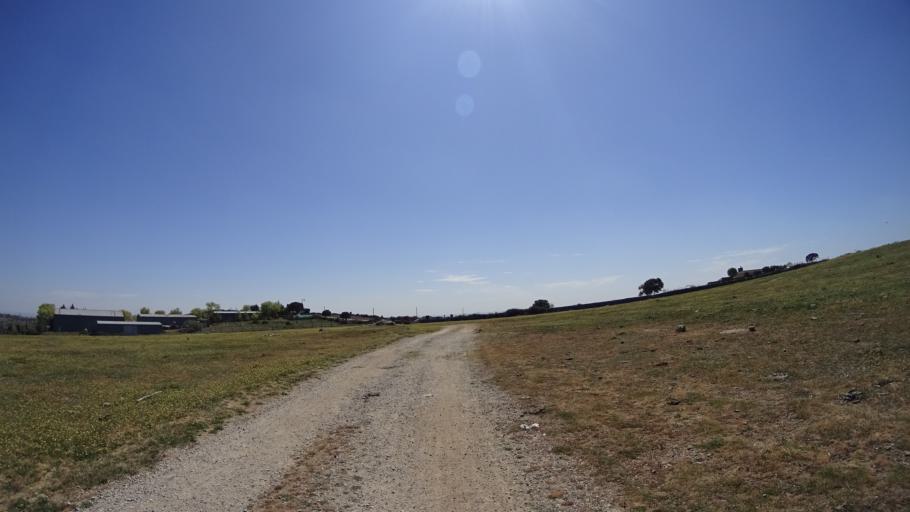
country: ES
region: Madrid
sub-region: Provincia de Madrid
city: Colmenar Viejo
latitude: 40.6902
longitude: -3.7556
